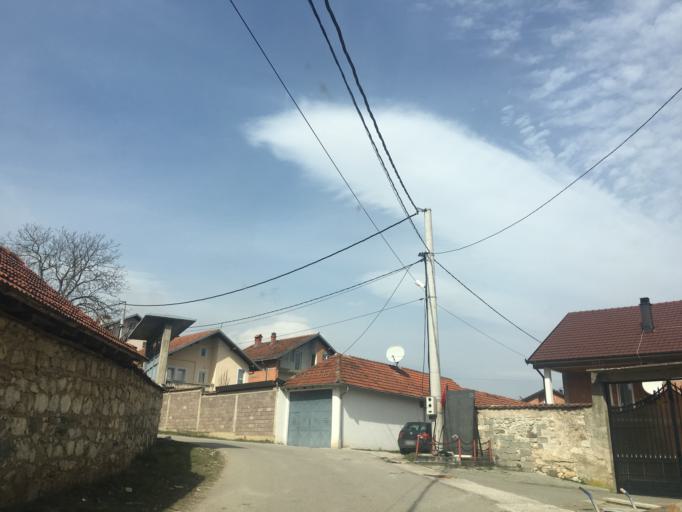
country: XK
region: Gjakova
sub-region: Komuna e Decanit
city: Strellc i Eperm
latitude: 42.5967
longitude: 20.2929
